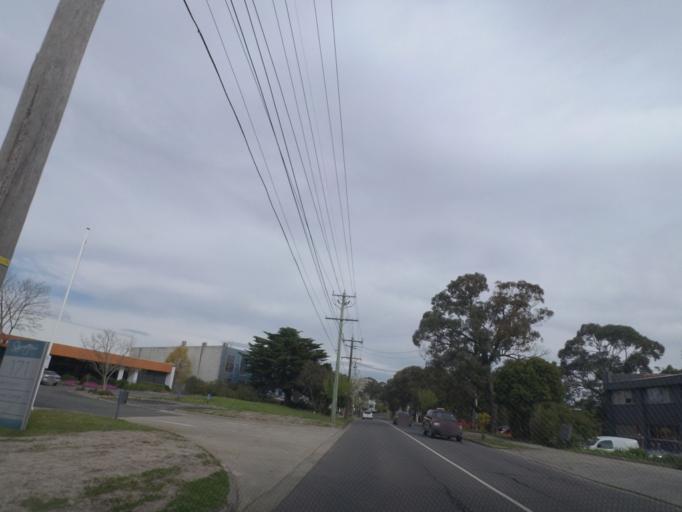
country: AU
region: Victoria
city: Forest Hill
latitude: -37.8337
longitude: 145.1878
